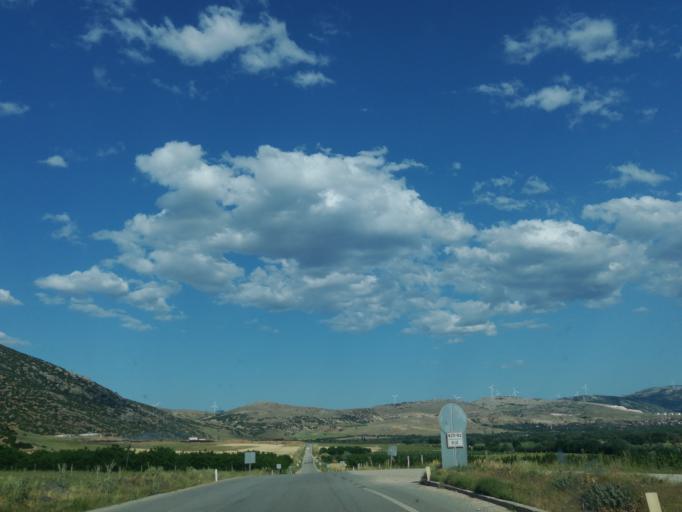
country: TR
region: Afyonkarahisar
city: Dinar
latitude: 38.1013
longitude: 30.1312
